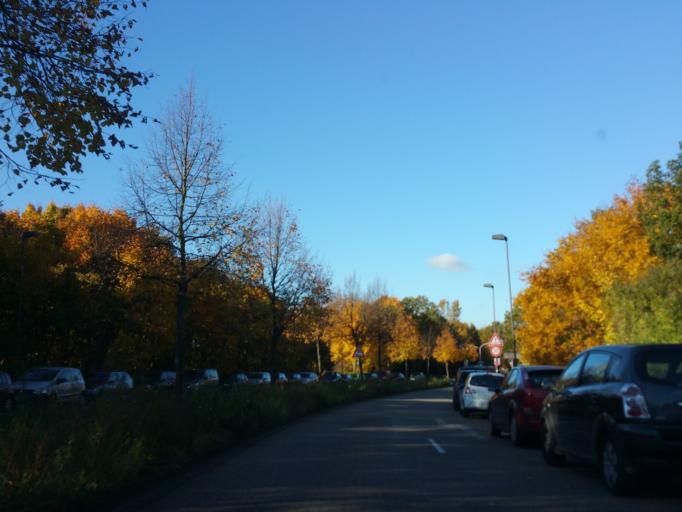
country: DE
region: North Rhine-Westphalia
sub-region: Regierungsbezirk Dusseldorf
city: Dusseldorf
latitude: 51.1868
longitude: 6.7937
